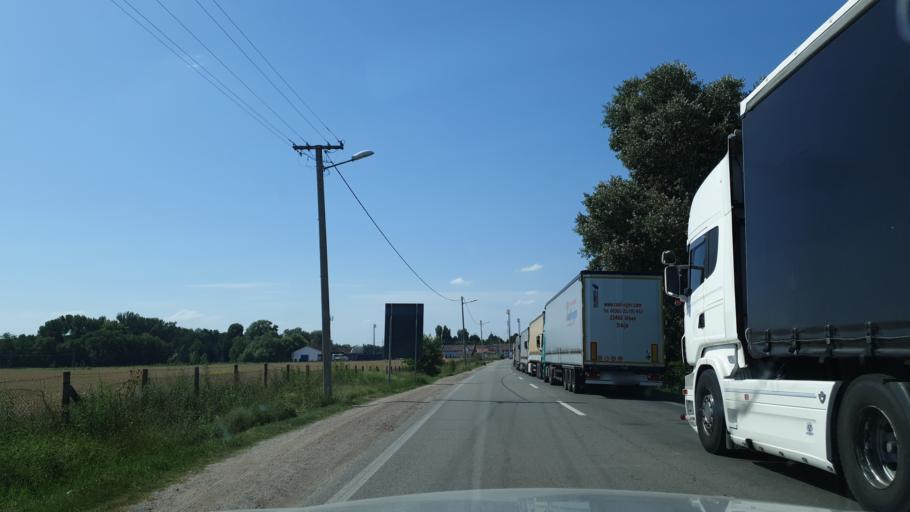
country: HU
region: Bacs-Kiskun
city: Tompa
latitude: 46.1616
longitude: 19.5657
